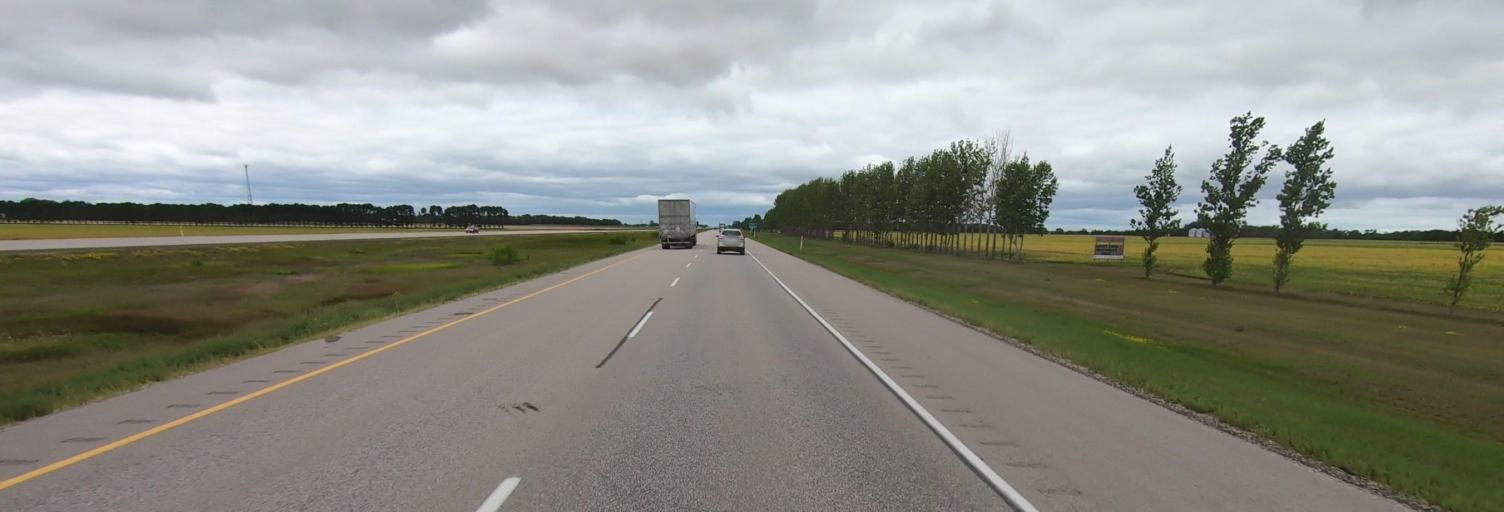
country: CA
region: Manitoba
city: Portage la Prairie
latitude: 49.9499
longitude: -97.9921
